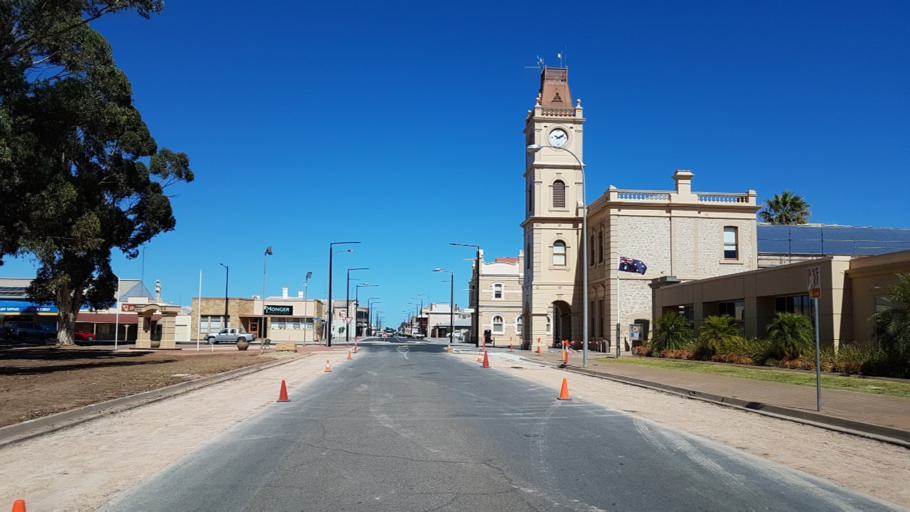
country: AU
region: South Australia
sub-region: Copper Coast
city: Kadina
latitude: -33.9619
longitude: 137.7154
